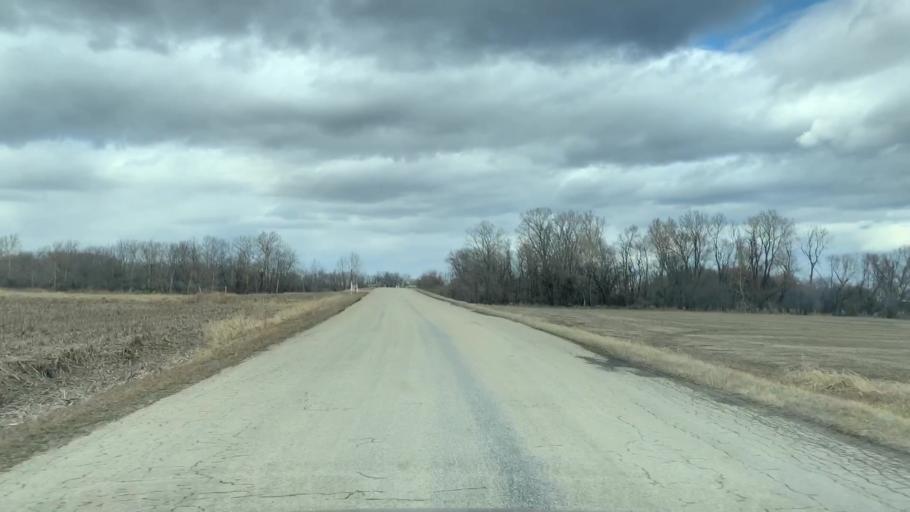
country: US
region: Kansas
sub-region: Allen County
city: Humboldt
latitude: 37.8024
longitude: -95.4707
